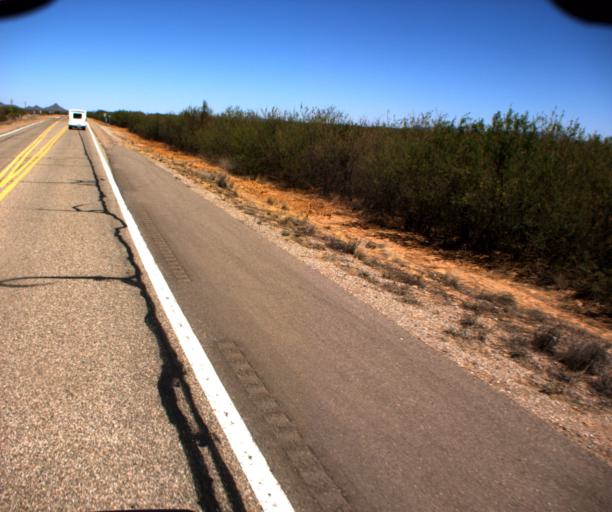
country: US
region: Arizona
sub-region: Pima County
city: Ajo
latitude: 32.1902
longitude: -112.4115
